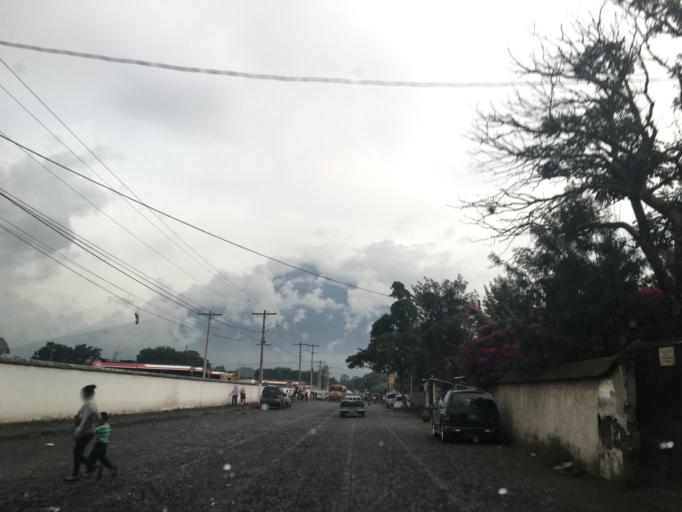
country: GT
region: Sacatepequez
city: Antigua Guatemala
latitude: 14.5601
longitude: -90.7406
